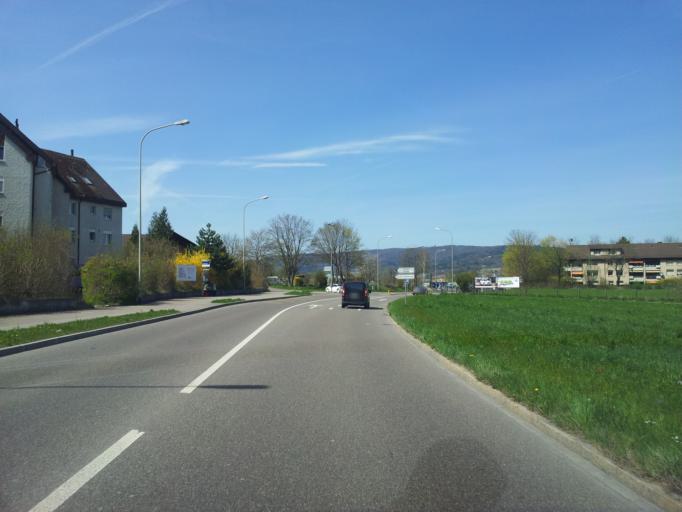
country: CH
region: Zurich
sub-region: Bezirk Dielsdorf
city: Regensdorf / Hofacher-Geeren
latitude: 47.4307
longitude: 8.4616
